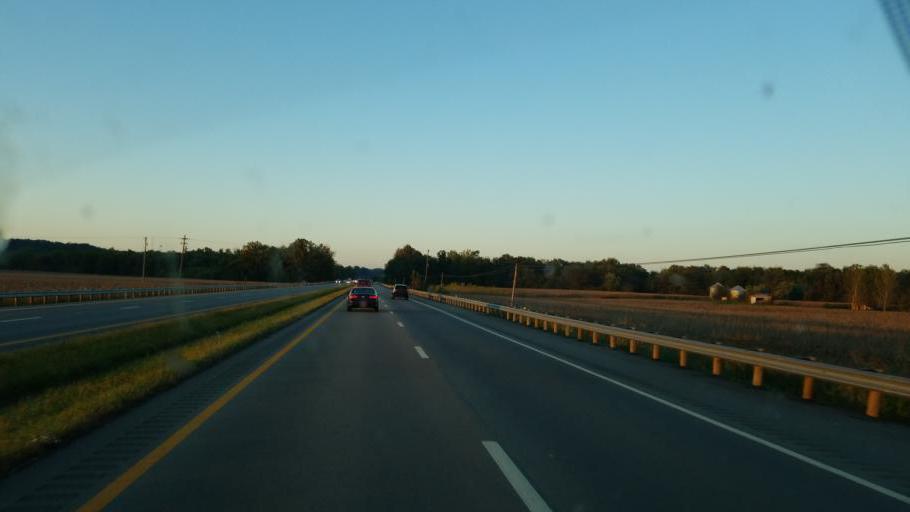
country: US
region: Ohio
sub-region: Pike County
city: Piketon
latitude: 39.0951
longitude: -83.0006
